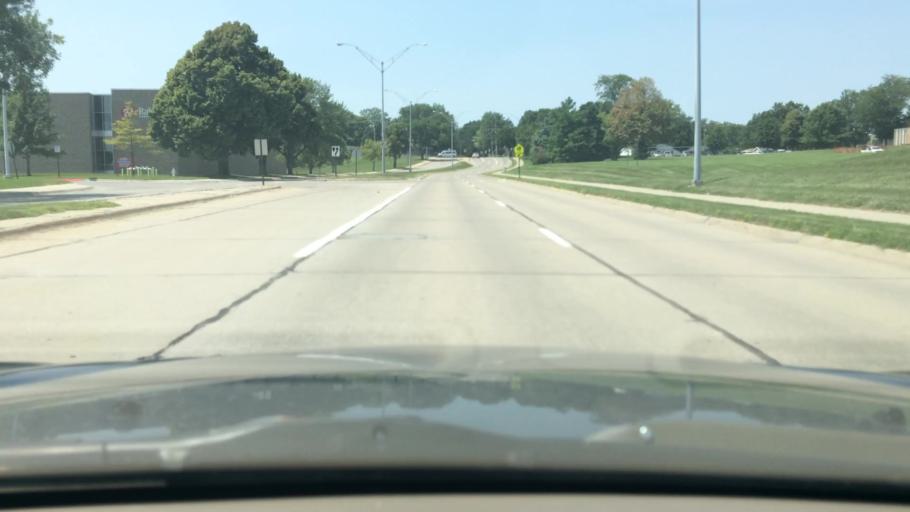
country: US
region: Nebraska
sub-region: Douglas County
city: Ralston
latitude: 41.2016
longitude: -96.0493
